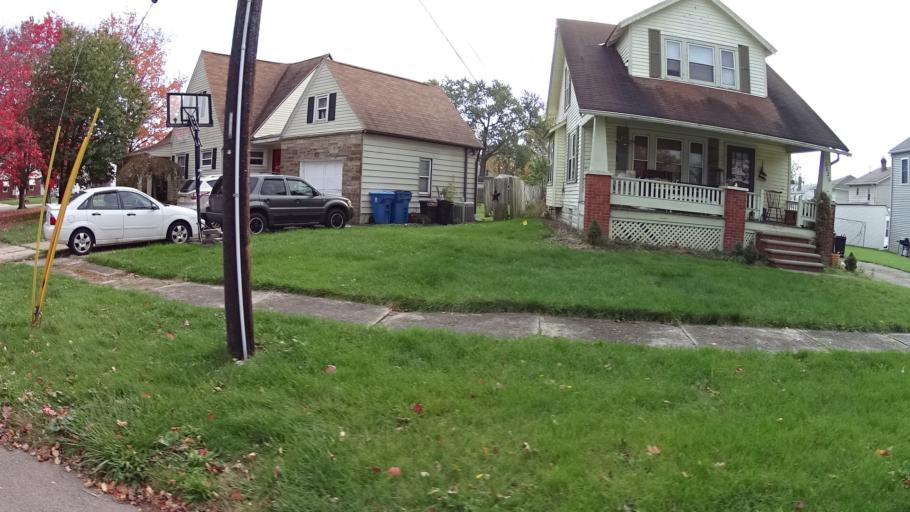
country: US
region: Ohio
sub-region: Lorain County
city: Sheffield Lake
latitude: 41.4801
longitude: -82.1385
